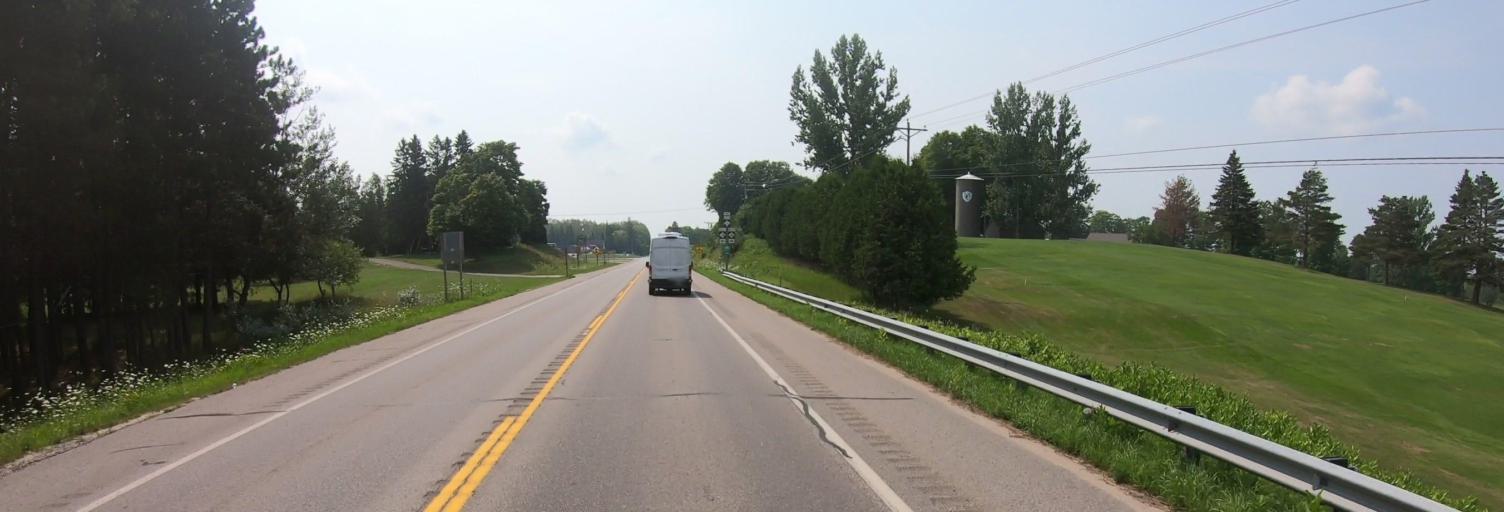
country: US
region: Michigan
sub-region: Luce County
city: Newberry
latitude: 46.3067
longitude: -85.5096
